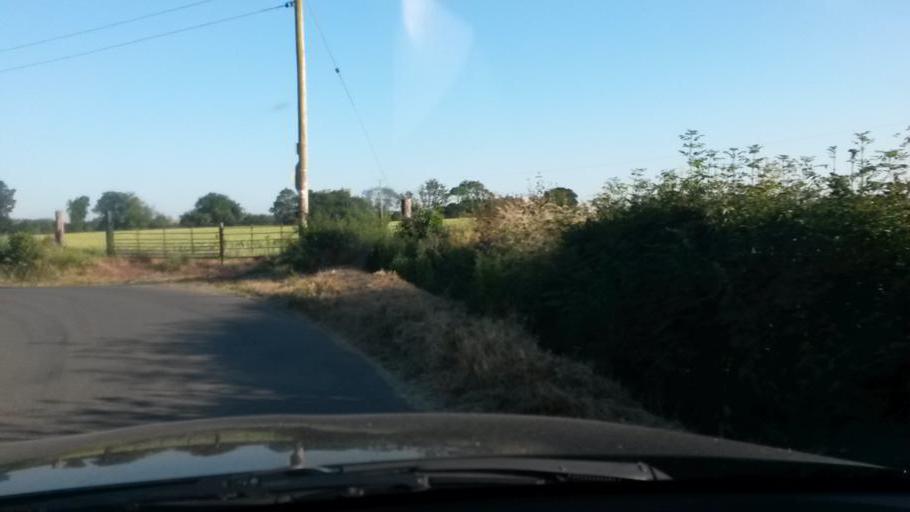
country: IE
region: Leinster
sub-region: Dublin City
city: Finglas
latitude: 53.4305
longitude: -6.3190
